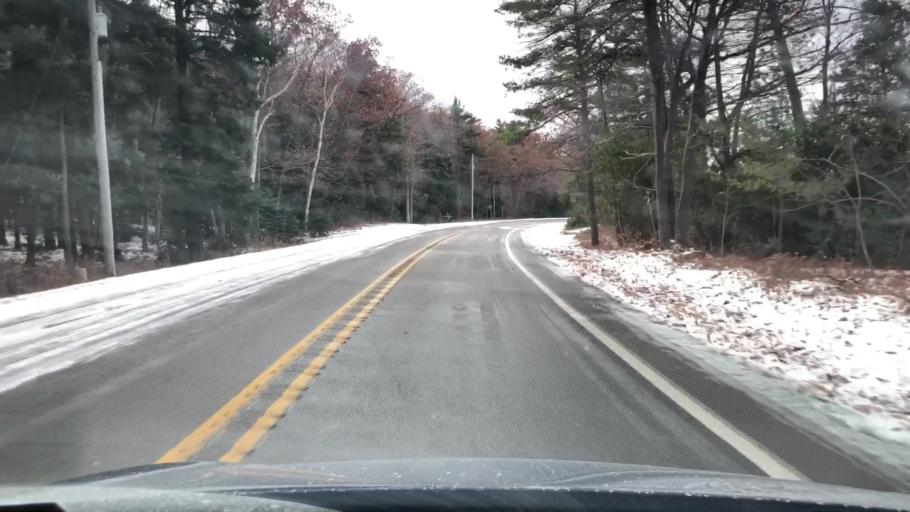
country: US
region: Michigan
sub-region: Antrim County
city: Elk Rapids
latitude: 44.9828
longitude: -85.4968
